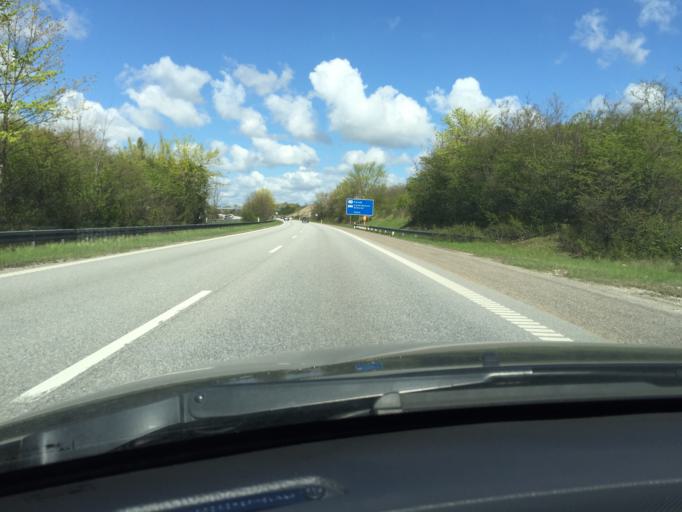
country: DK
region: Capital Region
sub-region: Fureso Kommune
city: Stavnsholt
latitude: 55.8162
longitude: 12.3837
